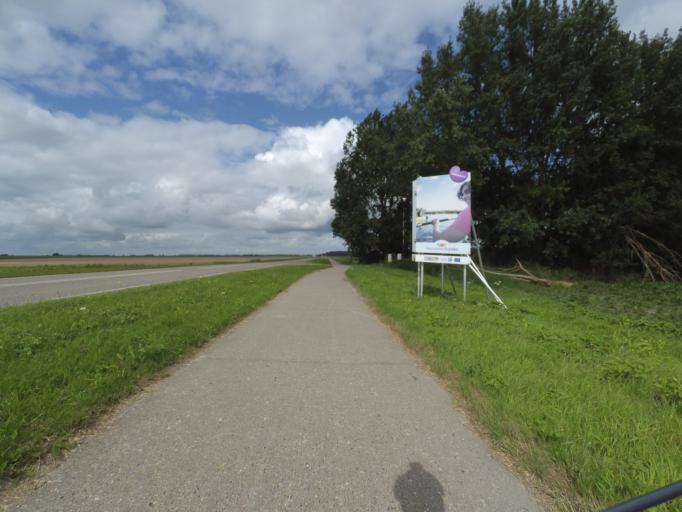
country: NL
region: Groningen
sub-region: Gemeente Zuidhorn
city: Grijpskerk
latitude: 53.3162
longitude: 6.2599
